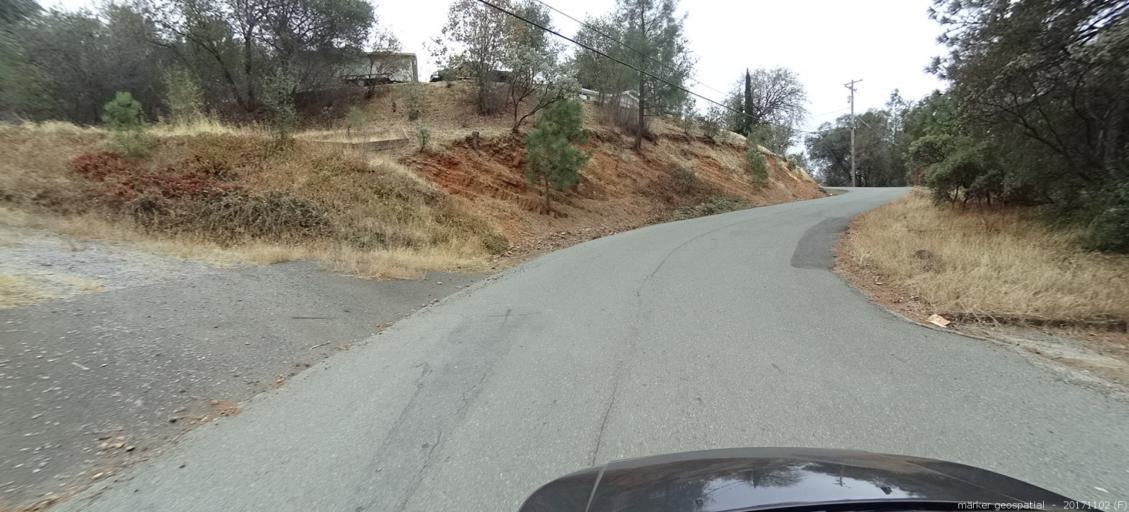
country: US
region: California
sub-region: Shasta County
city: Bella Vista
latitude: 40.7179
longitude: -122.2401
